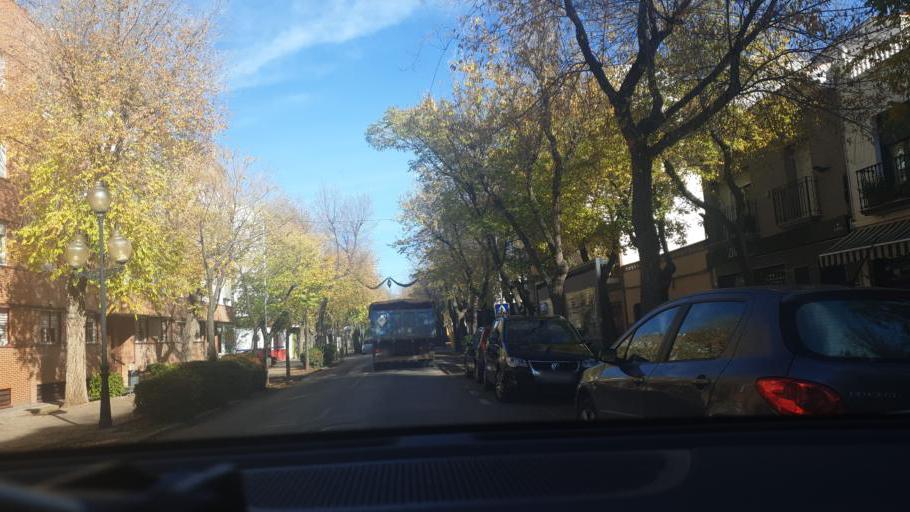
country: ES
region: Castille-La Mancha
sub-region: Provincia de Ciudad Real
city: Tomelloso
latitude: 39.1516
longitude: -3.0144
